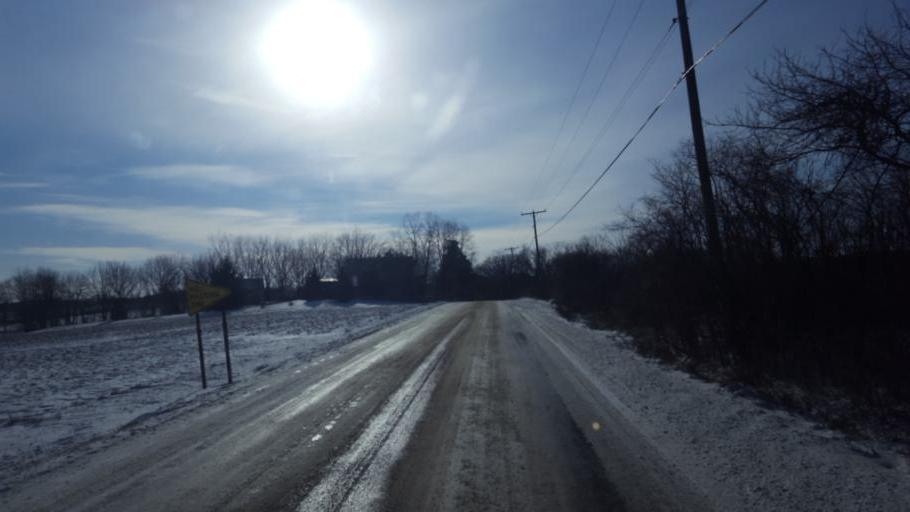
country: US
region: Ohio
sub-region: Morrow County
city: Mount Gilead
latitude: 40.5742
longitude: -82.7197
